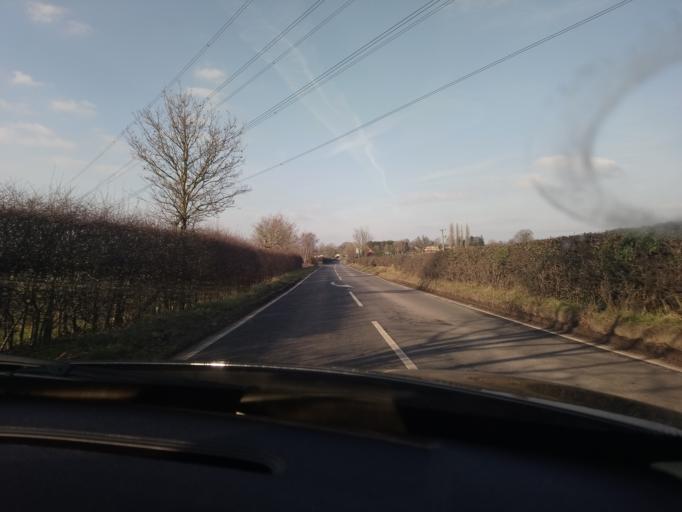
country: GB
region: England
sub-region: Shropshire
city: Bicton
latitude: 52.7641
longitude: -2.7786
